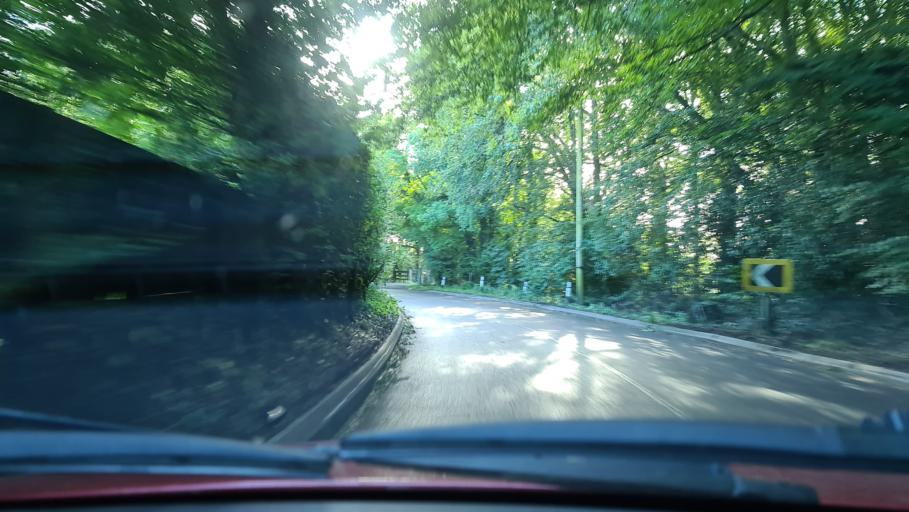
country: GB
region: England
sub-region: Oxfordshire
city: Chinnor
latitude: 51.6872
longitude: -0.8881
